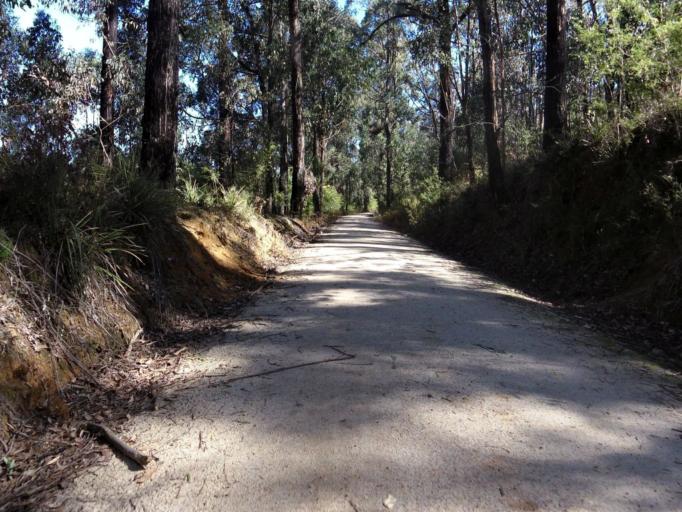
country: AU
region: Victoria
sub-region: Latrobe
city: Moe
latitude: -38.3865
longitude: 146.1893
